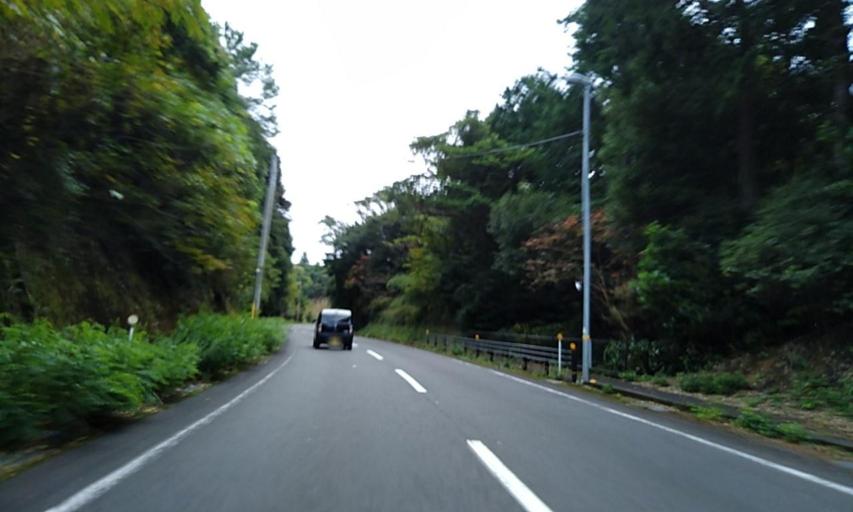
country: JP
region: Wakayama
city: Shingu
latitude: 33.4672
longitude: 135.8270
